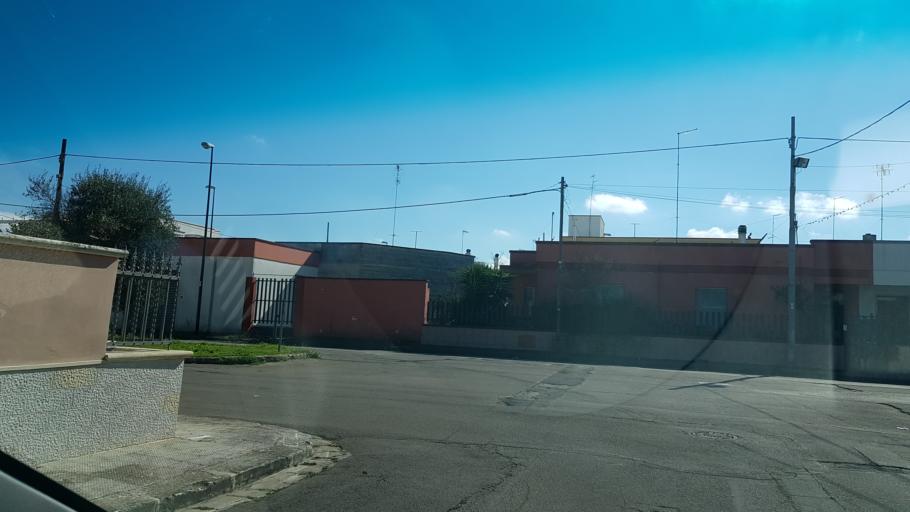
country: IT
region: Apulia
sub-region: Provincia di Lecce
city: Campi Salentina
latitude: 40.3940
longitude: 18.0097
